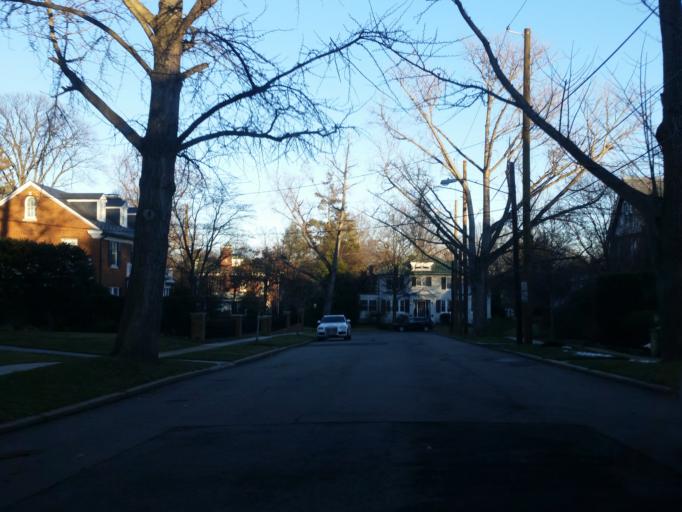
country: US
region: Maryland
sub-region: Montgomery County
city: Chevy Chase Village
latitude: 38.9563
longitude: -77.0755
